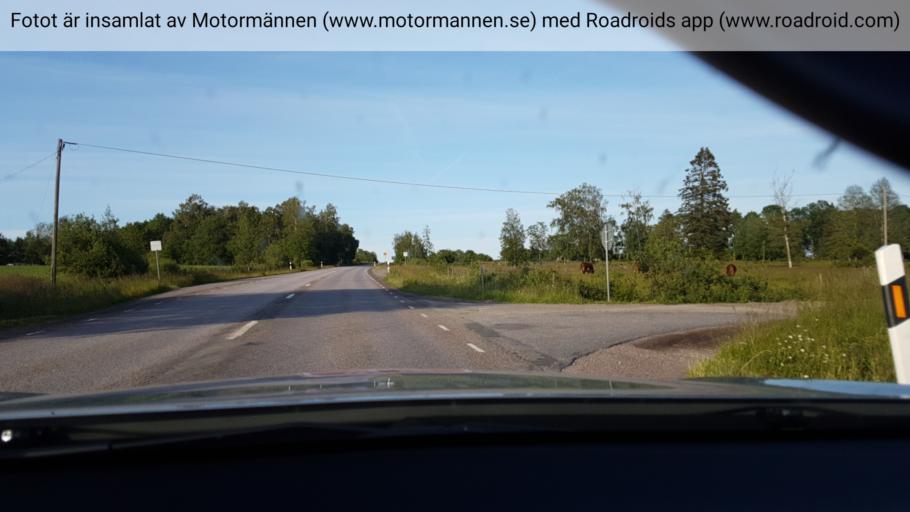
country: SE
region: Vaestra Goetaland
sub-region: Skovde Kommun
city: Skultorp
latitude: 58.2887
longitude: 13.7751
